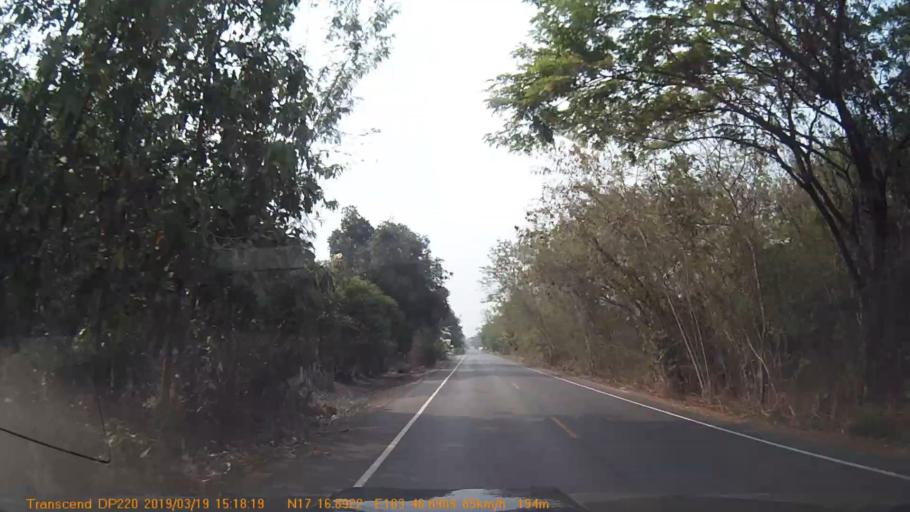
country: TH
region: Sakon Nakhon
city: Phanna Nikhom
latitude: 17.2819
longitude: 103.7780
